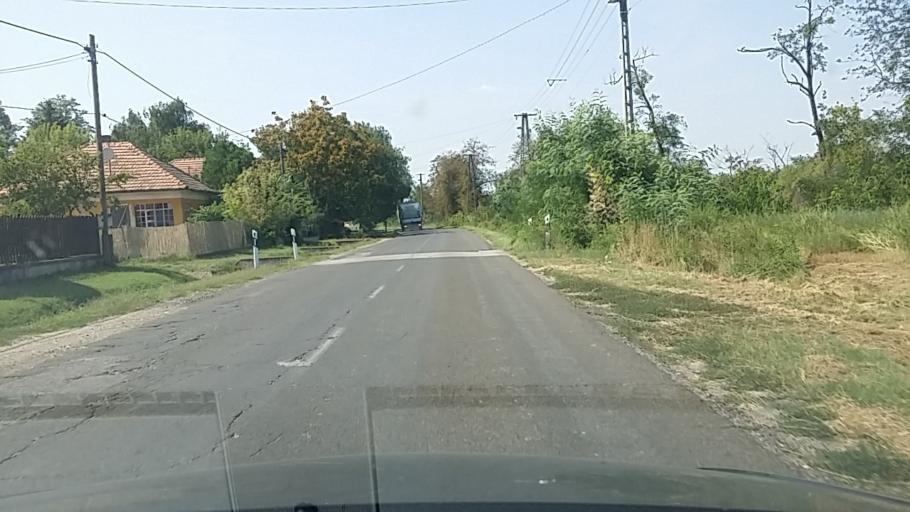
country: HU
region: Pest
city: Tapiobicske
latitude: 47.3551
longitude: 19.6987
